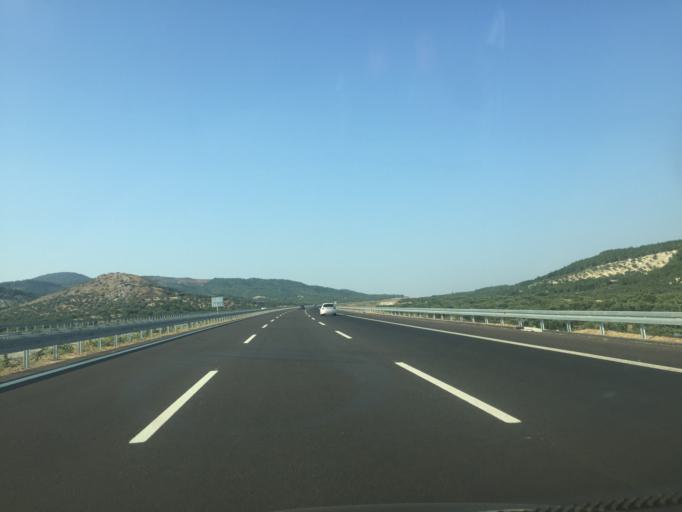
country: TR
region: Manisa
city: Zeytinliova
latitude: 38.9850
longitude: 27.7318
